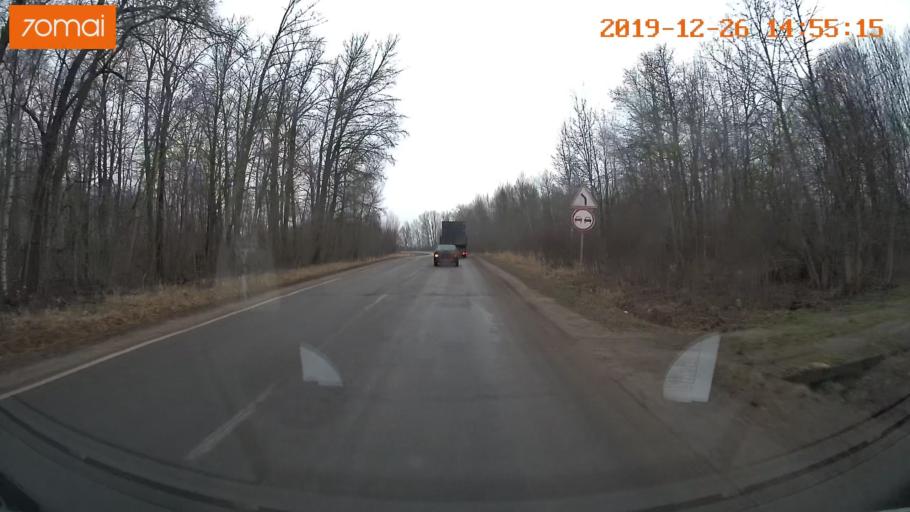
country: RU
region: Jaroslavl
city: Rybinsk
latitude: 58.3019
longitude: 38.8769
